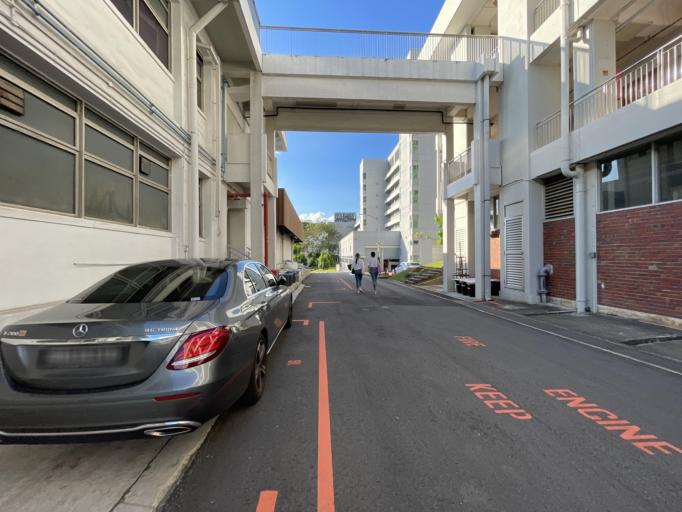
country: SG
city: Singapore
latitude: 1.2988
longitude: 103.7709
